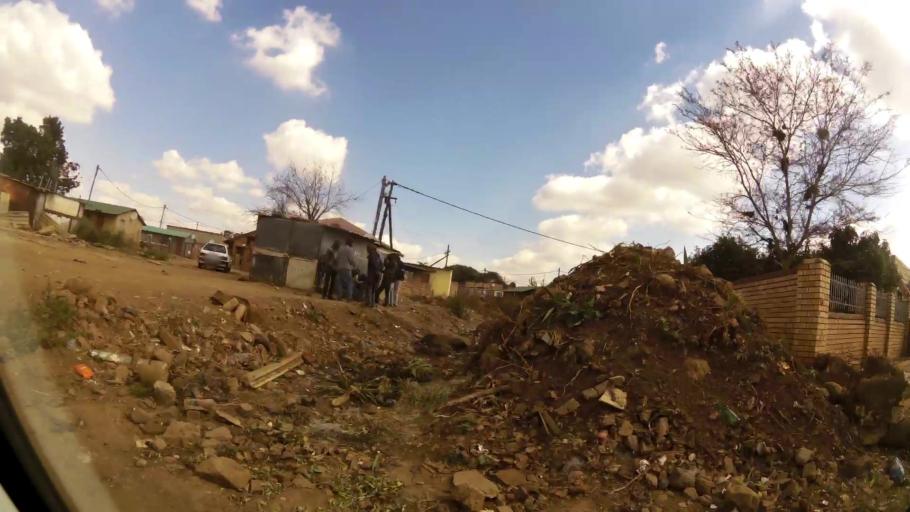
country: ZA
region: Gauteng
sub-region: City of Tshwane Metropolitan Municipality
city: Cullinan
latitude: -25.7076
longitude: 28.3978
